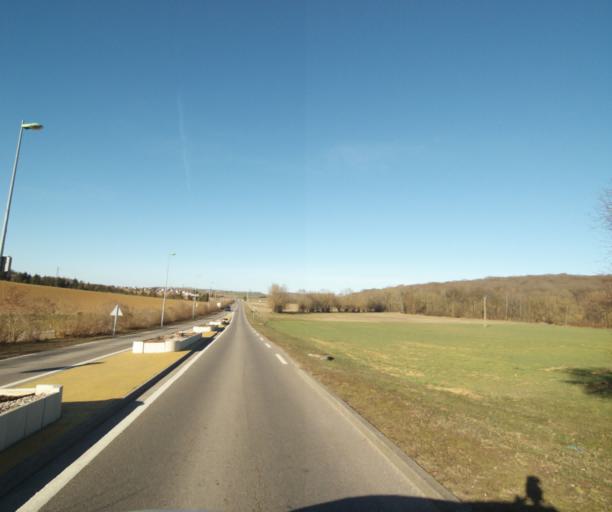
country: FR
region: Lorraine
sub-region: Departement de Meurthe-et-Moselle
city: Fleville-devant-Nancy
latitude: 48.6313
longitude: 6.2102
